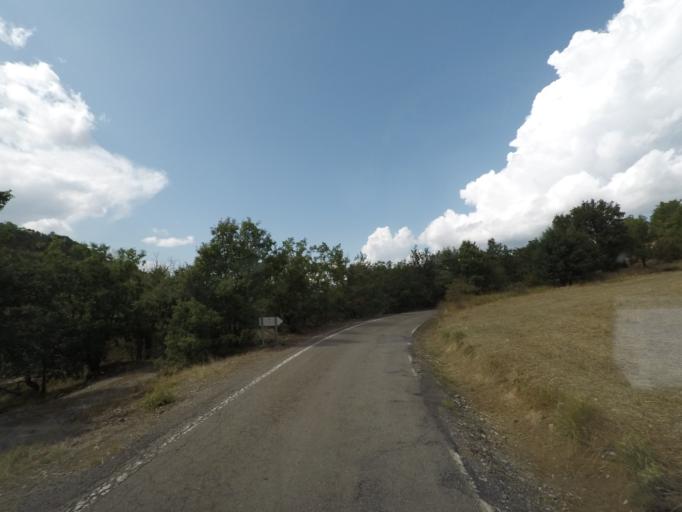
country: ES
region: Aragon
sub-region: Provincia de Huesca
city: Yebra de Basa
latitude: 42.3943
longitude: -0.3244
